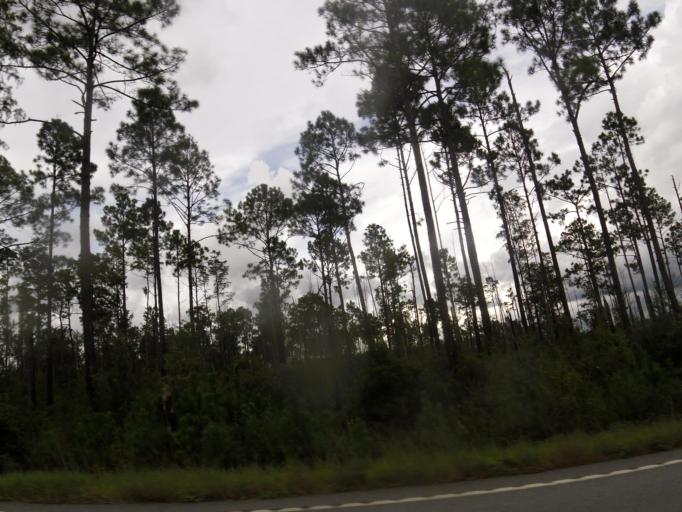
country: US
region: Florida
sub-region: Baker County
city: Macclenny
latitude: 30.5239
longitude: -82.1605
